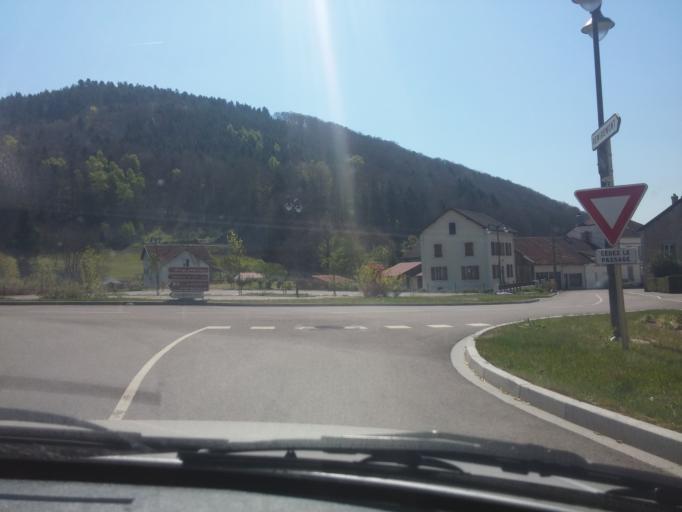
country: FR
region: Lorraine
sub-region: Departement des Vosges
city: Plombieres-les-Bains
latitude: 47.9270
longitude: 6.4898
